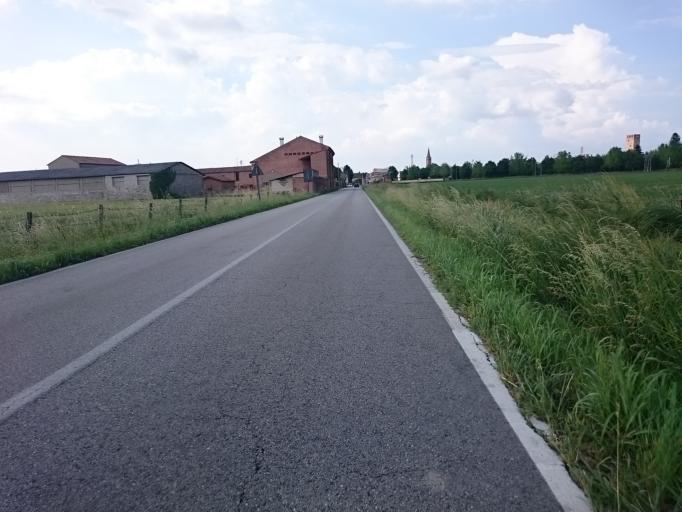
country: IT
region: Veneto
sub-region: Provincia di Padova
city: Montagnana
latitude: 45.2250
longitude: 11.4684
